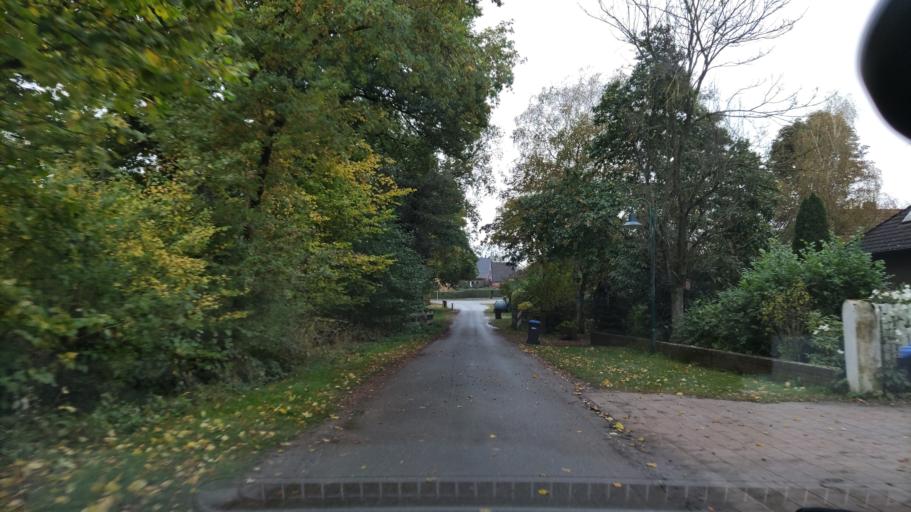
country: DE
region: Lower Saxony
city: Deutsch Evern
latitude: 53.1975
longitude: 10.4427
